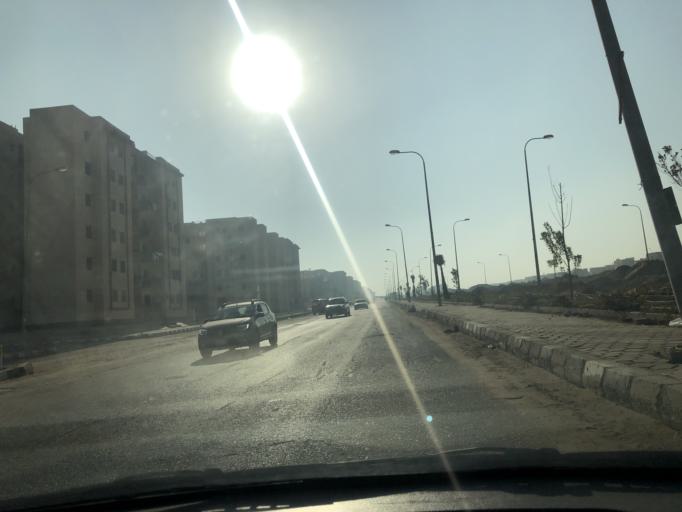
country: EG
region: Al Jizah
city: Madinat Sittah Uktubar
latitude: 29.9259
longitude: 31.0328
